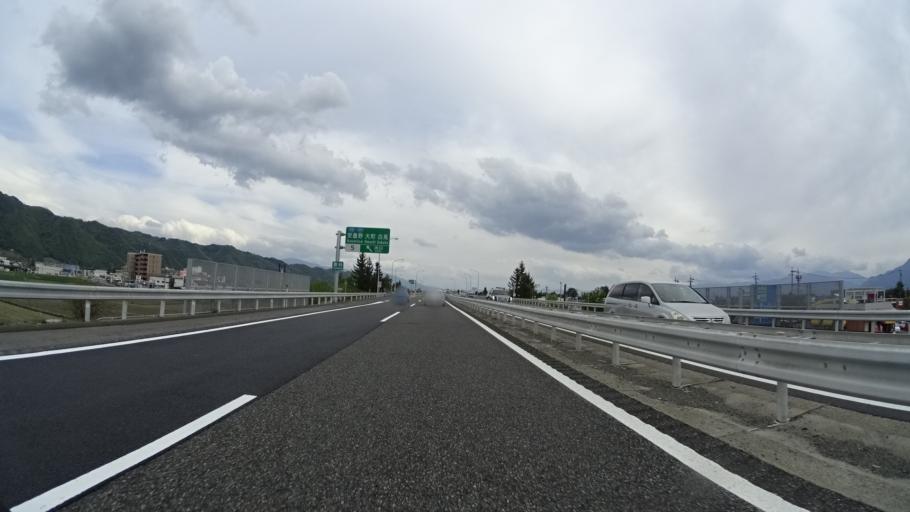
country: JP
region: Nagano
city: Toyoshina
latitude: 36.3018
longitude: 137.9239
